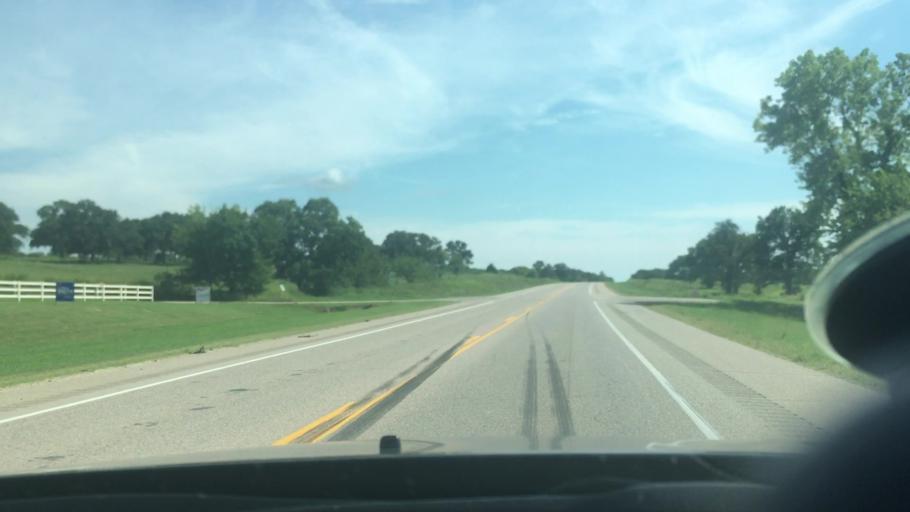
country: US
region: Oklahoma
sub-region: Seminole County
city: Seminole
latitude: 35.1747
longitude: -96.6741
